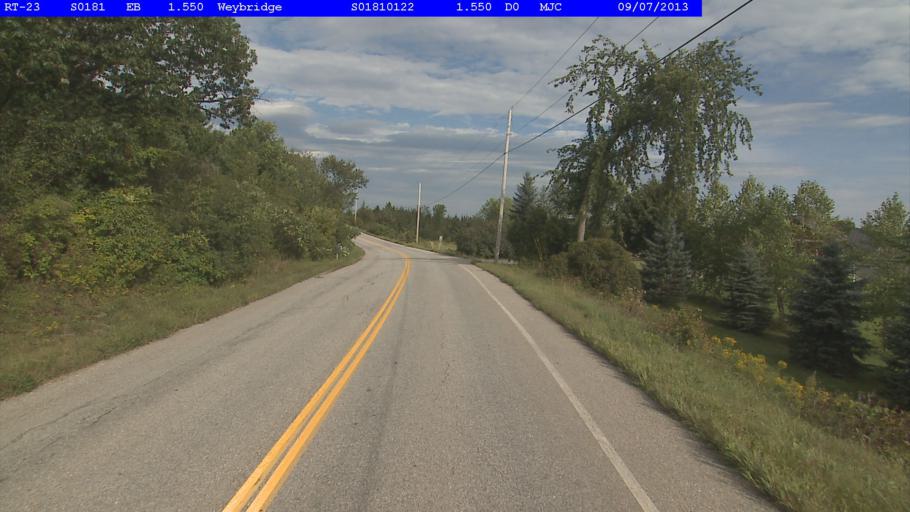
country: US
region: Vermont
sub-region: Addison County
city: Middlebury (village)
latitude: 44.0341
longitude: -73.2048
